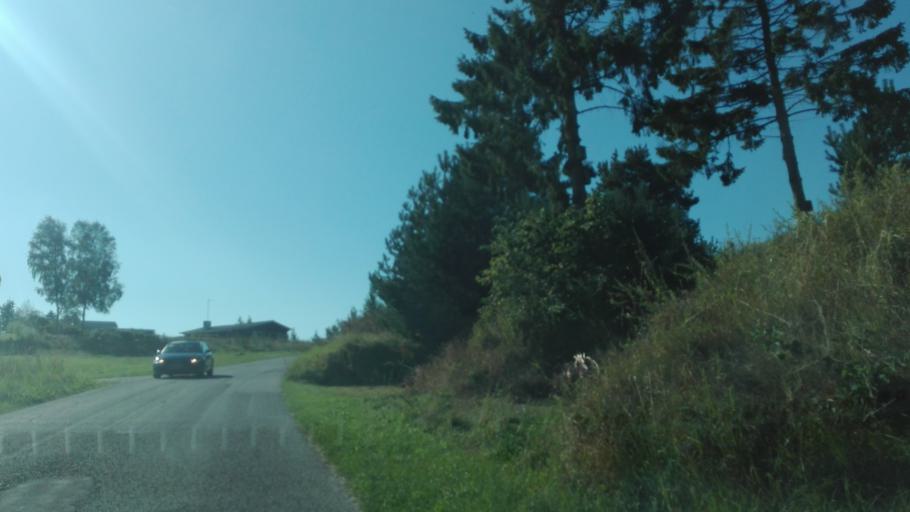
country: DK
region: Central Jutland
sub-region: Syddjurs Kommune
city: Ebeltoft
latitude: 56.2481
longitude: 10.6243
